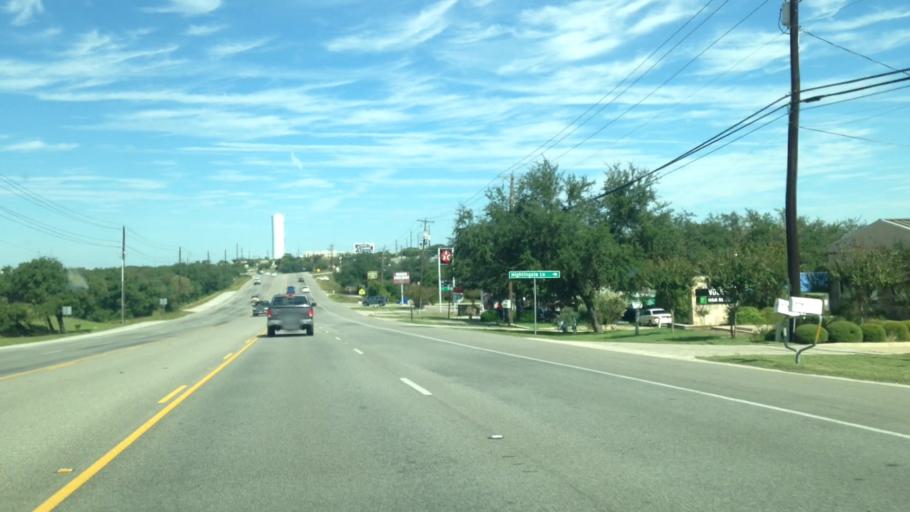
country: US
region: Texas
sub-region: Travis County
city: Lakeway
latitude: 30.3659
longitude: -97.9509
